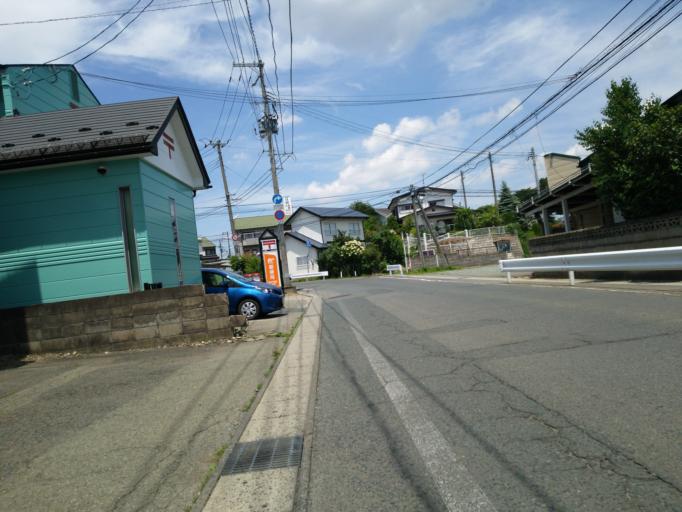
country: JP
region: Iwate
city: Morioka-shi
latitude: 39.7106
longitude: 141.1197
